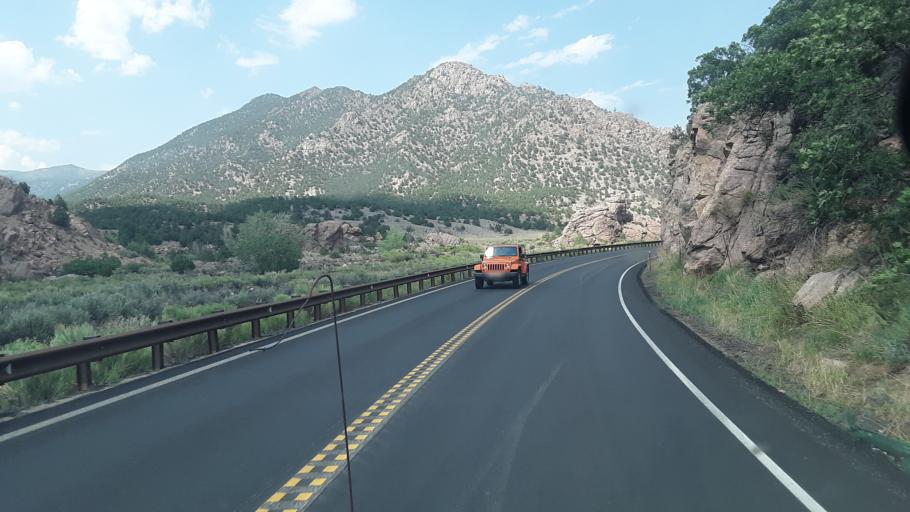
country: US
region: Colorado
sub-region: Fremont County
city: Canon City
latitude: 38.4416
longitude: -105.5403
